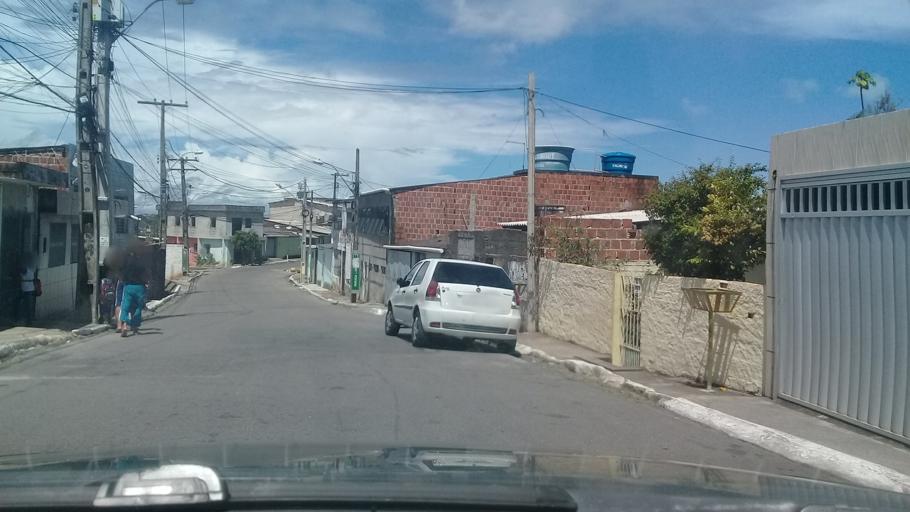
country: BR
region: Pernambuco
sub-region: Jaboatao Dos Guararapes
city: Jaboatao dos Guararapes
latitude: -8.1251
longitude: -34.9468
